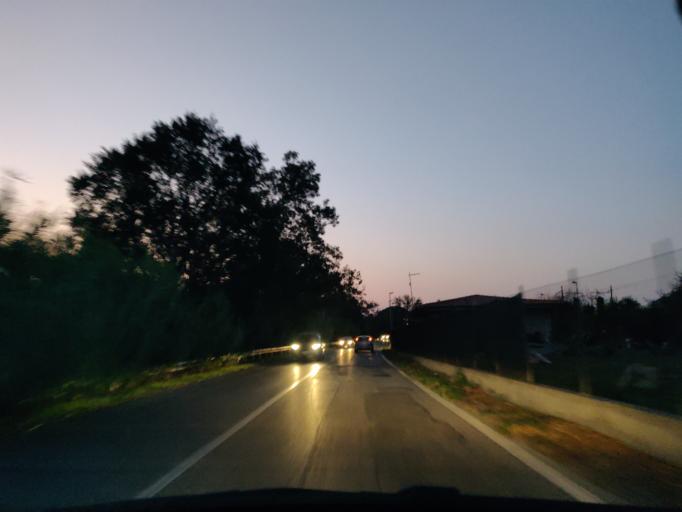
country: IT
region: Latium
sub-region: Citta metropolitana di Roma Capitale
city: Npp 23 (Parco Leonardo)
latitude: 41.8469
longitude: 12.2688
